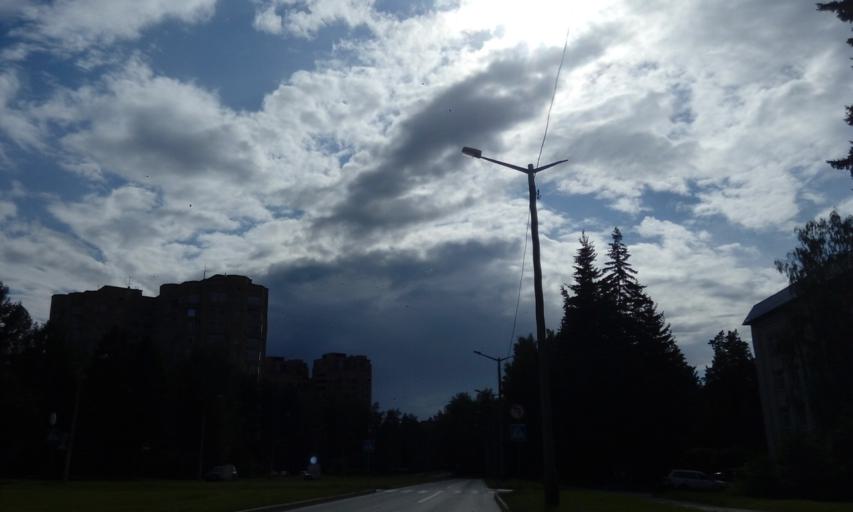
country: RU
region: Novosibirsk
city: Akademgorodok
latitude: 54.8464
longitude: 83.1049
